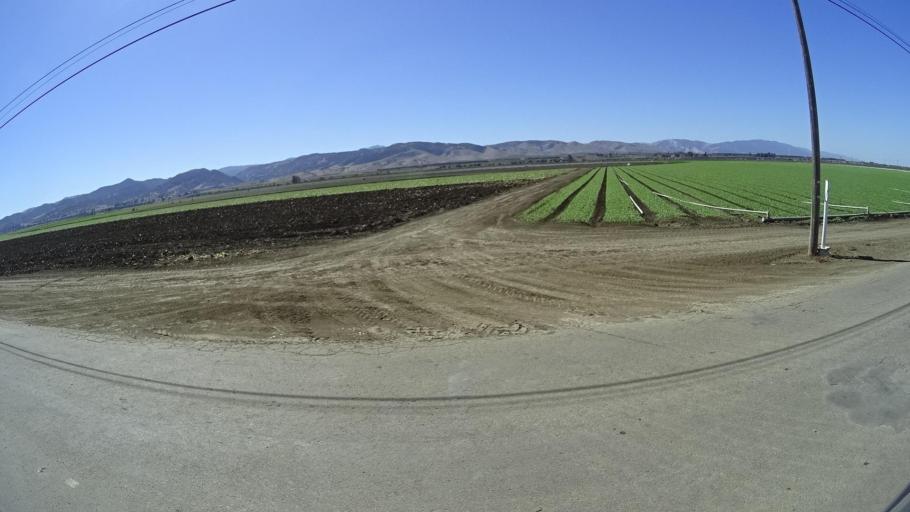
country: US
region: California
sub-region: Monterey County
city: King City
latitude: 36.2565
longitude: -121.1507
